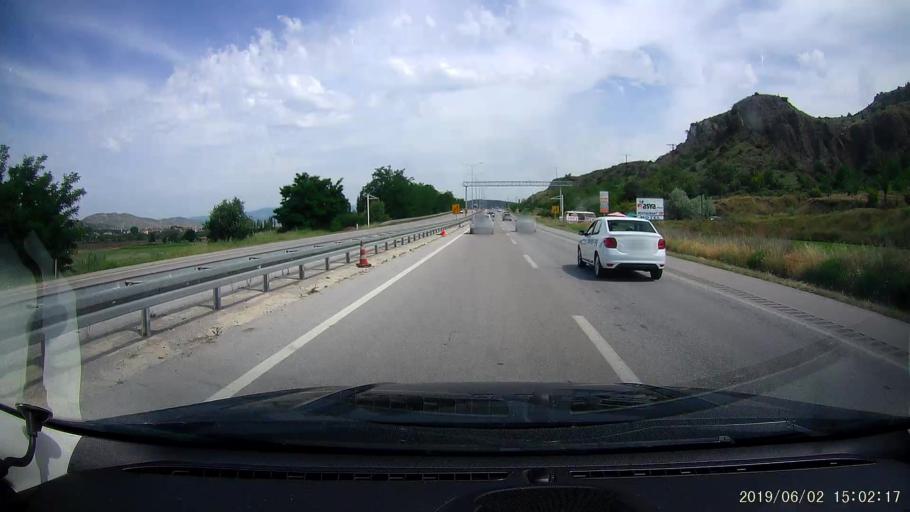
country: TR
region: Corum
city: Osmancik
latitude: 40.9823
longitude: 34.7649
